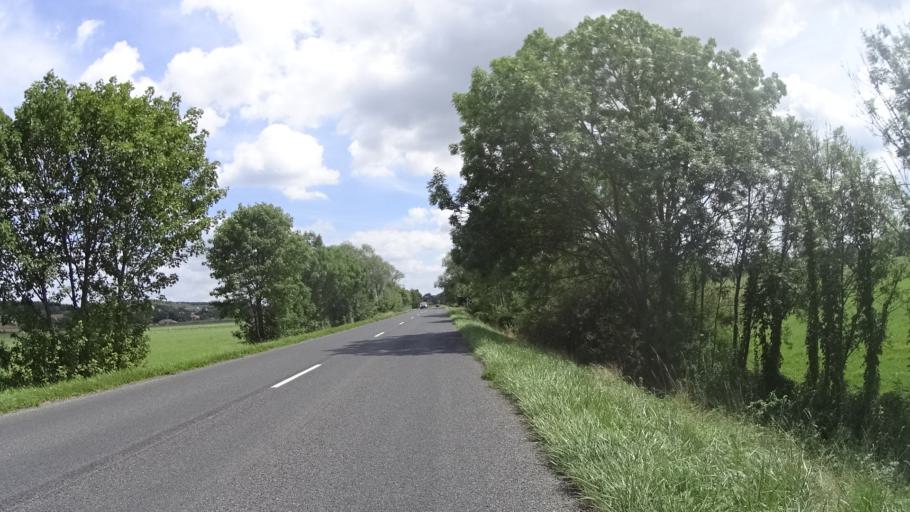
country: FR
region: Lorraine
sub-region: Departement de la Meuse
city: Euville
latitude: 48.7555
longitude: 5.6135
